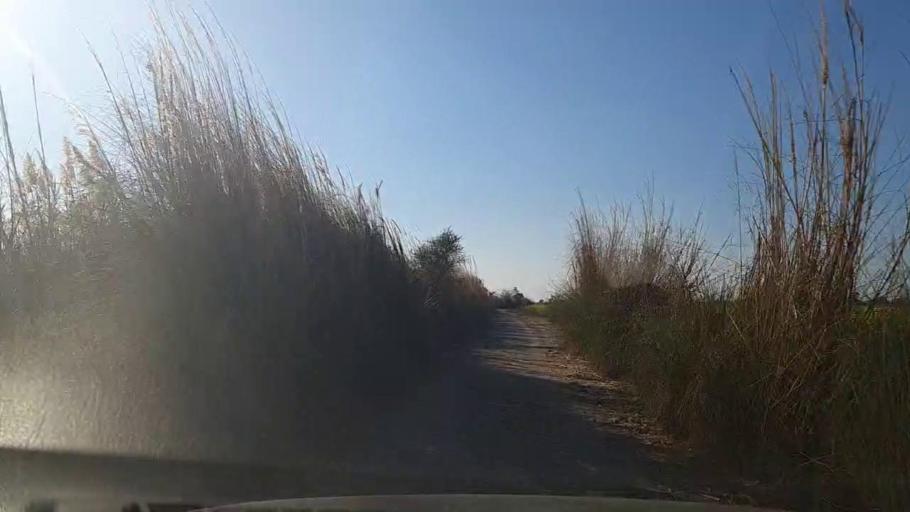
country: PK
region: Sindh
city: Khadro
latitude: 26.2412
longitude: 68.8674
